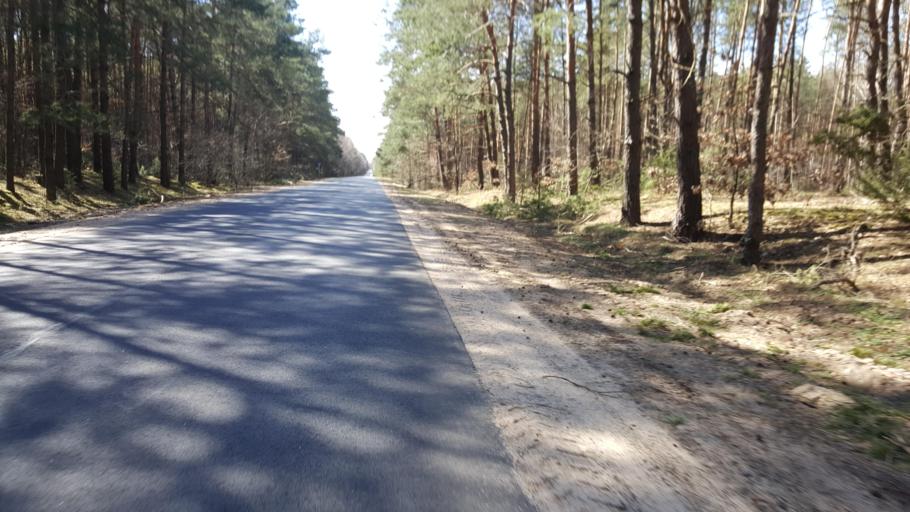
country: BY
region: Brest
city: Charnawchytsy
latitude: 52.2915
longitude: 23.8063
